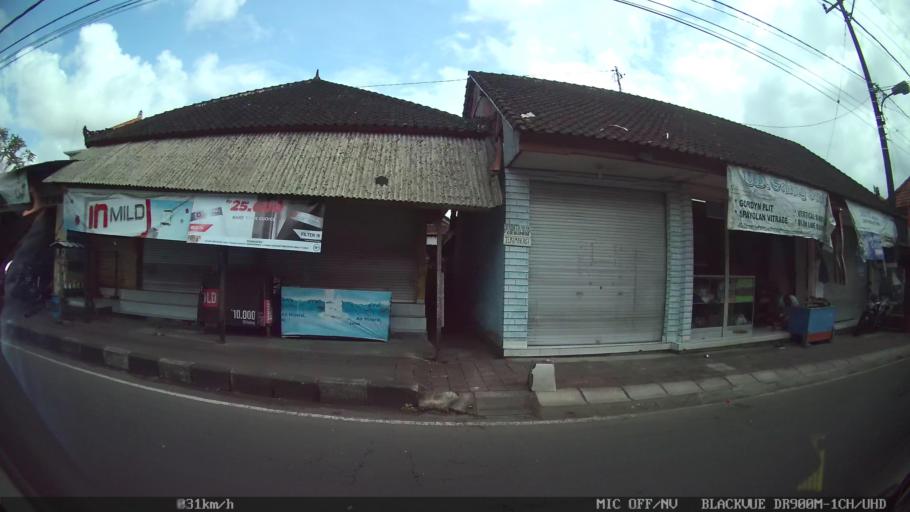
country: ID
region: Bali
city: Banjar Pekenjelodan
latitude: -8.5814
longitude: 115.1882
